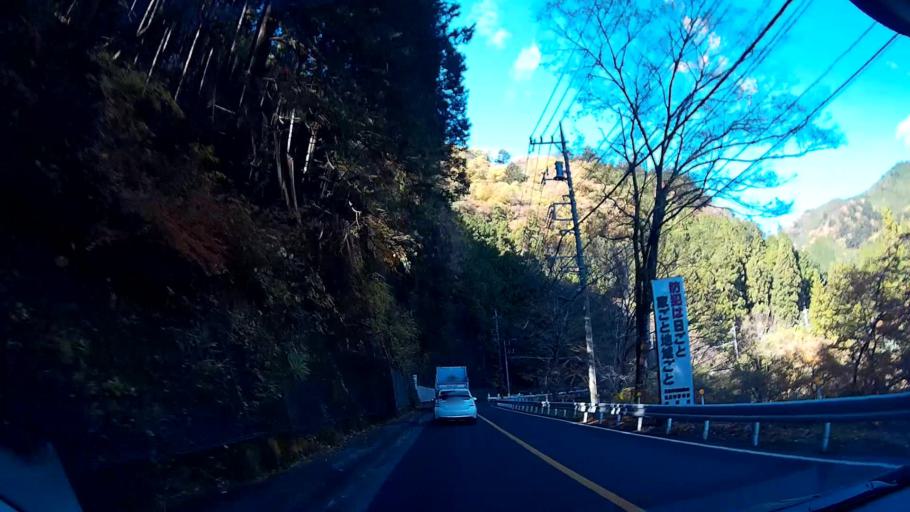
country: JP
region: Tokyo
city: Itsukaichi
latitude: 35.7238
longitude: 139.1596
